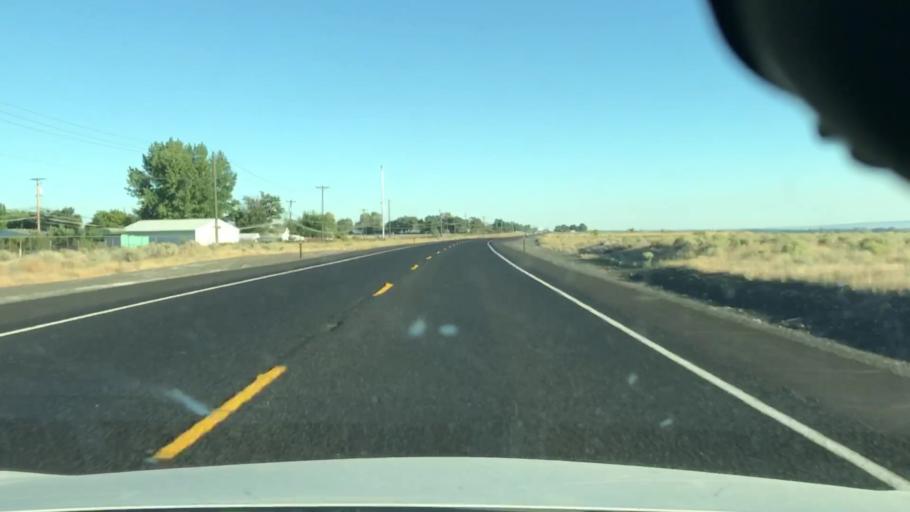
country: US
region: Washington
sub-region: Grant County
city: Moses Lake North
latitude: 47.1762
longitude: -119.3316
